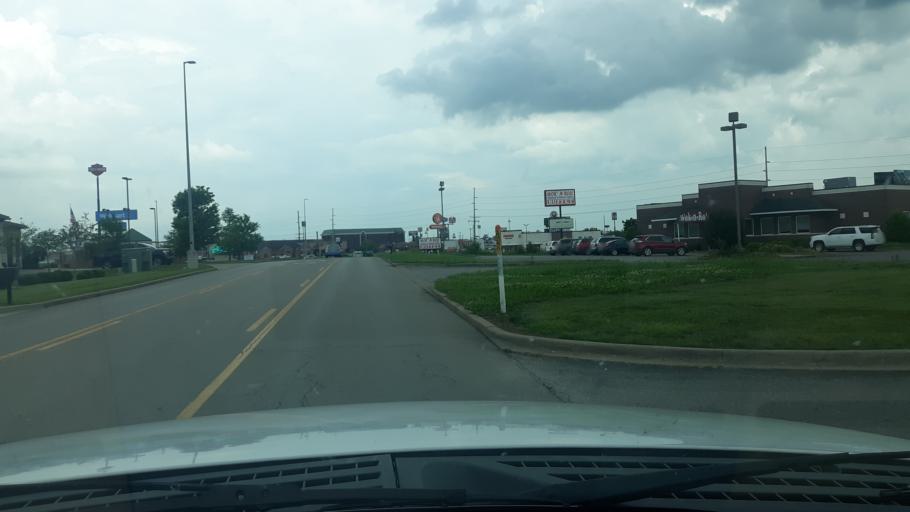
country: US
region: Illinois
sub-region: Williamson County
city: Marion
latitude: 37.7458
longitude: -88.9731
